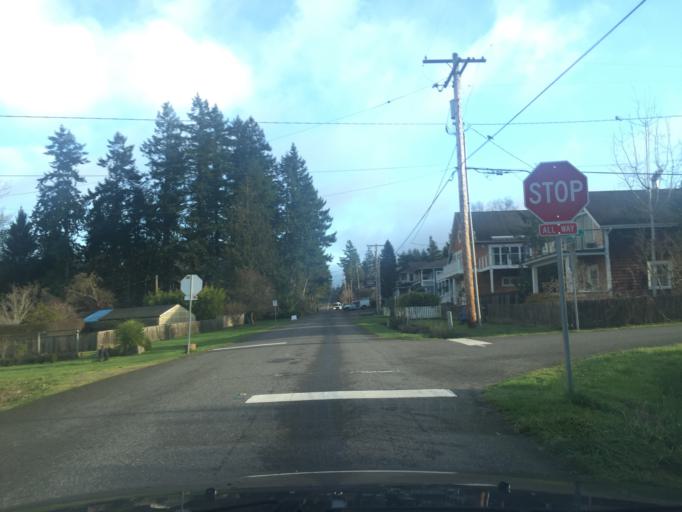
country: US
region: Washington
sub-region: Thurston County
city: Olympia
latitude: 47.1394
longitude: -122.9040
